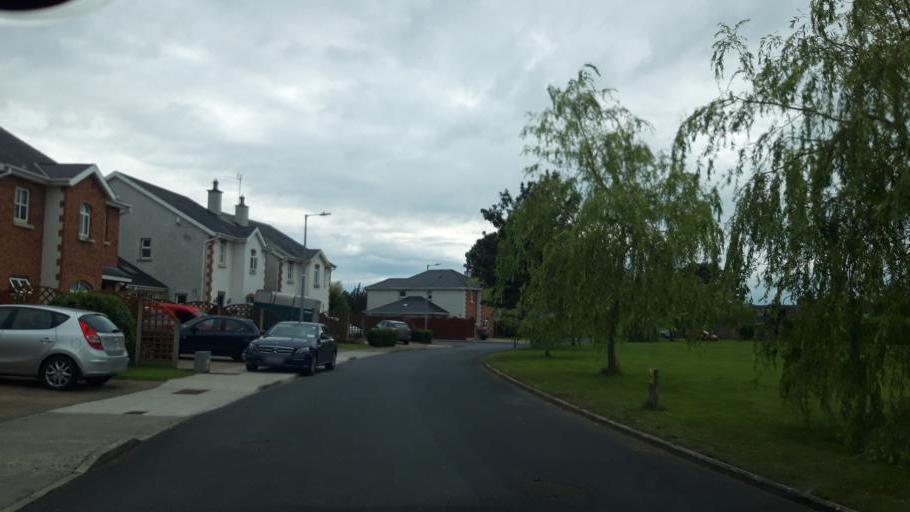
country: IE
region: Leinster
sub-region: Kilkenny
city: Ballyragget
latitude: 52.7883
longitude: -7.3295
